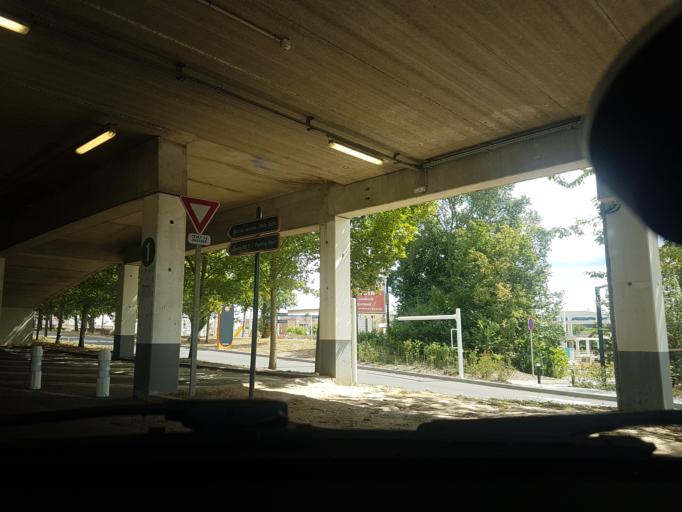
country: FR
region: Ile-de-France
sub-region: Departement des Yvelines
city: Plaisir
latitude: 48.8278
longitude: 1.9583
